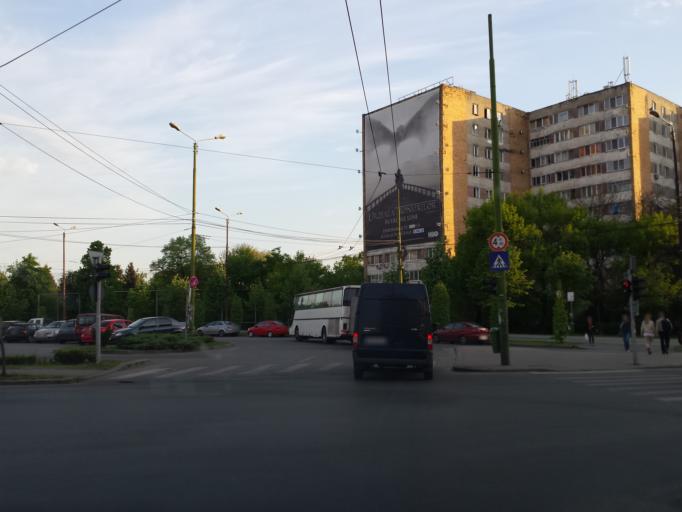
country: RO
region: Timis
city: Timisoara
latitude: 45.7644
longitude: 21.2247
